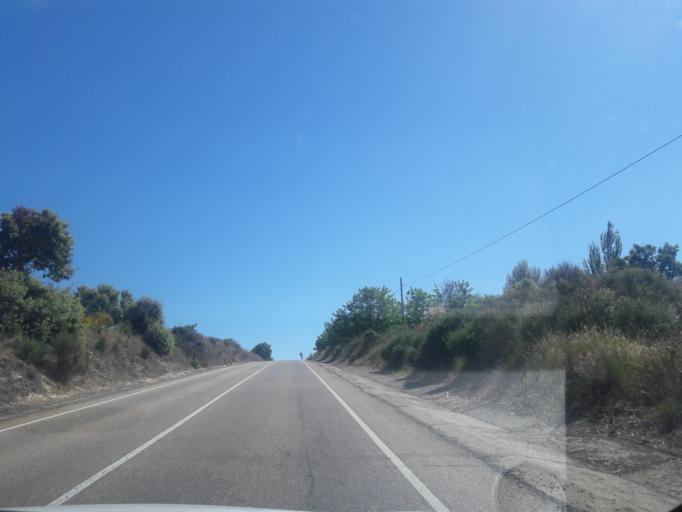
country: ES
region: Castille and Leon
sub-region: Provincia de Salamanca
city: Bermellar
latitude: 40.9600
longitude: -6.6478
